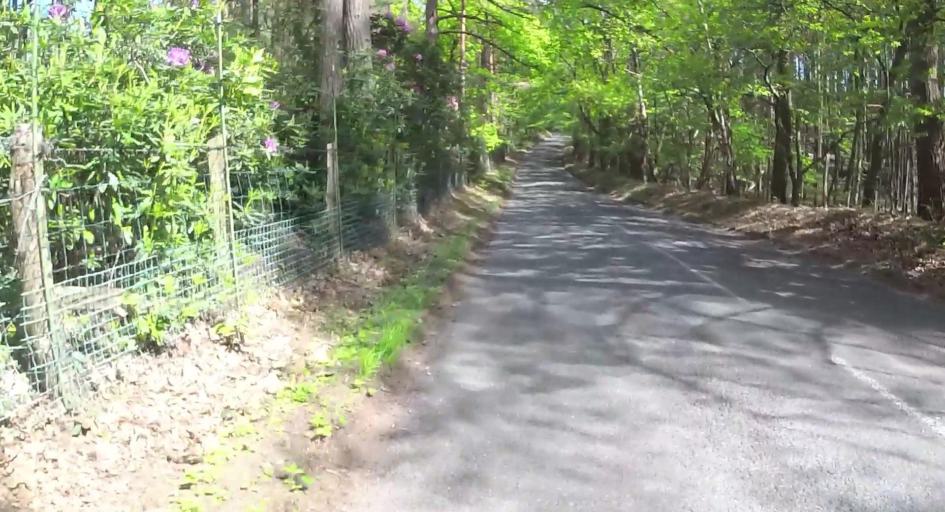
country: GB
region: England
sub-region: Surrey
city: Farnham
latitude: 51.1863
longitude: -0.7838
